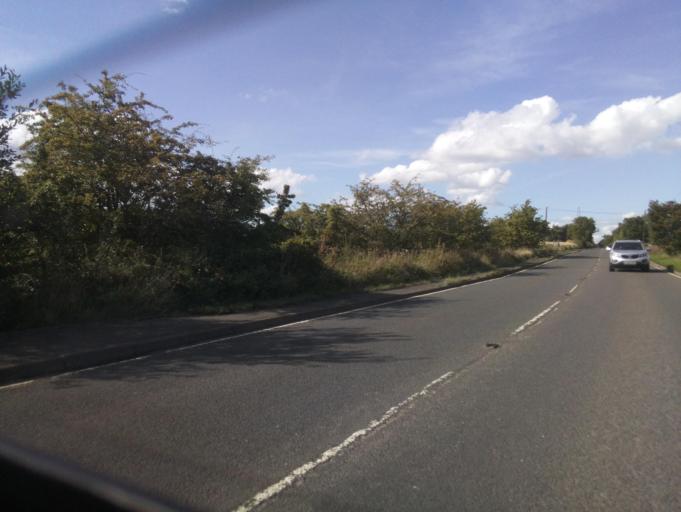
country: GB
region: Scotland
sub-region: Stirling
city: Cowie
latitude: 56.0505
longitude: -3.8581
